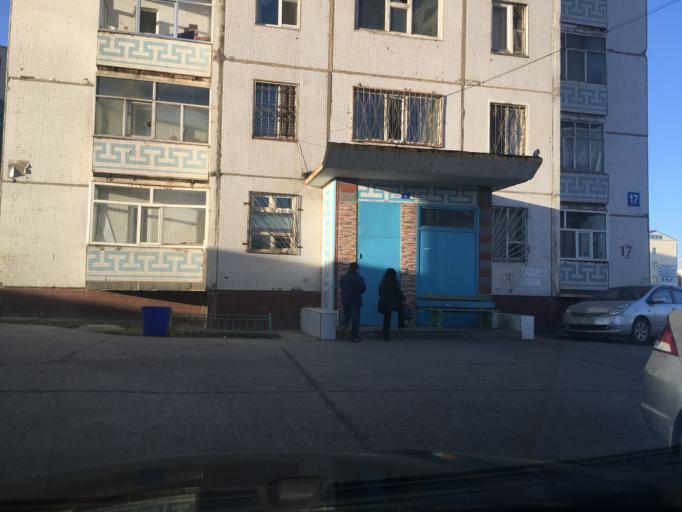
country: MN
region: Ulaanbaatar
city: Ulaanbaatar
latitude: 47.9247
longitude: 106.8823
